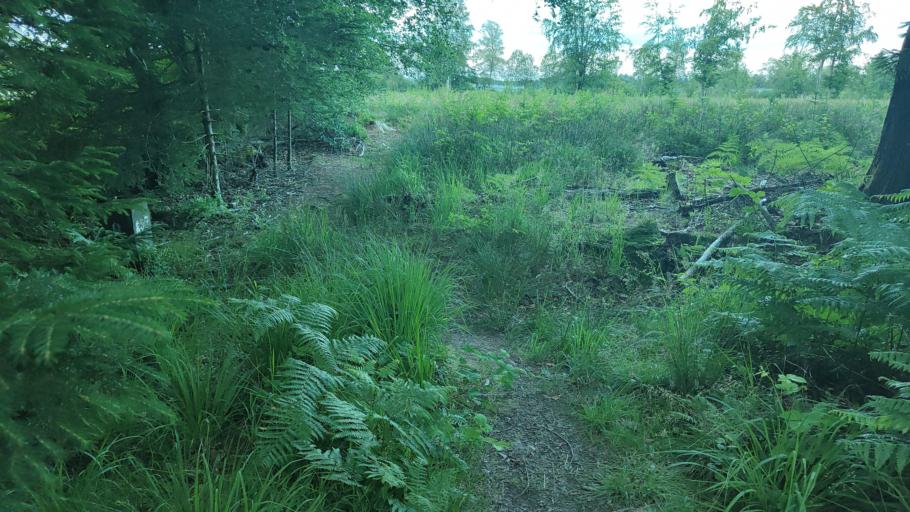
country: DE
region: North Rhine-Westphalia
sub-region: Regierungsbezirk Koln
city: Roetgen
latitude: 50.6330
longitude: 6.1808
